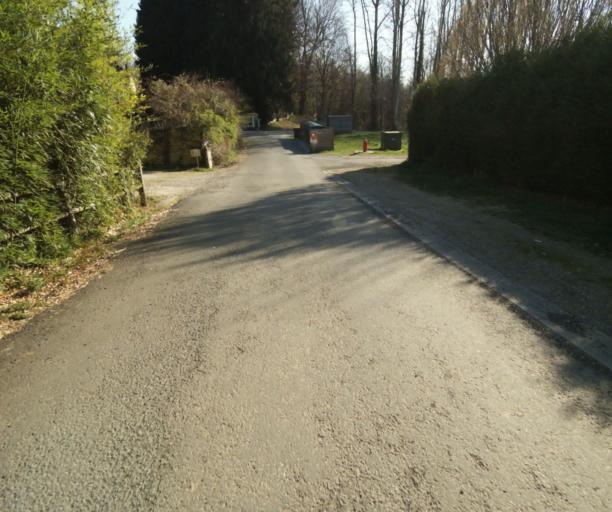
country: FR
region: Limousin
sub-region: Departement de la Correze
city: Saint-Clement
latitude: 45.3423
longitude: 1.6813
